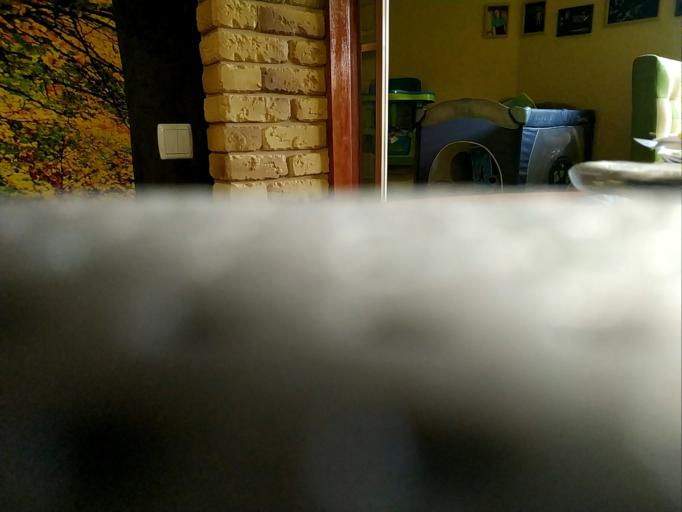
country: RU
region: Kaluga
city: Seredeyskiy
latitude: 53.8808
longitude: 35.3627
